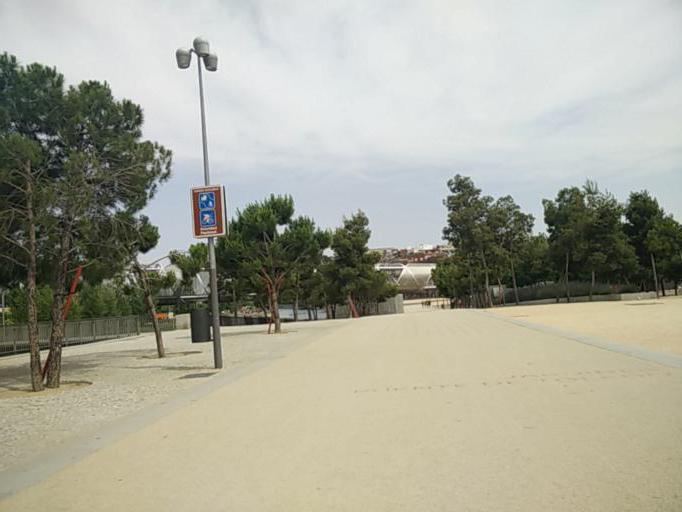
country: ES
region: Madrid
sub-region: Provincia de Madrid
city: Carabanchel
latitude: 40.3984
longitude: -3.7134
